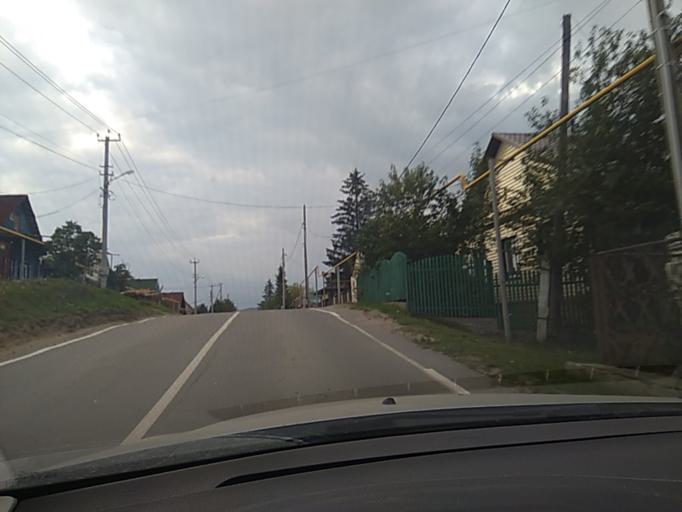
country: RU
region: Chelyabinsk
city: Kyshtym
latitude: 55.6990
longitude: 60.5360
